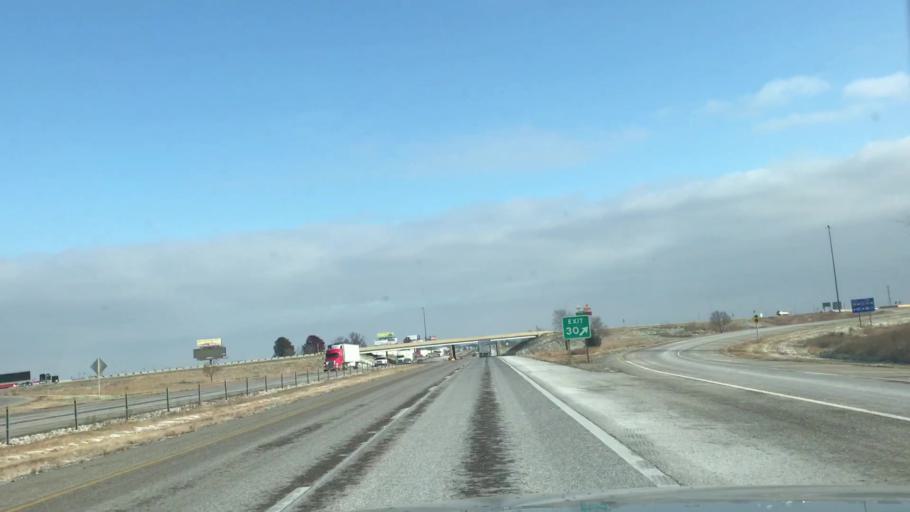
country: US
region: Illinois
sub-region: Madison County
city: Worden
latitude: 38.8867
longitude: -89.8397
